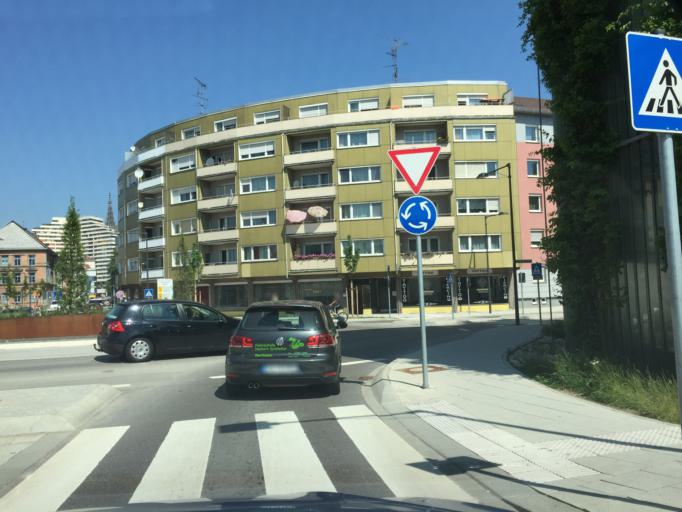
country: DE
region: Bavaria
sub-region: Swabia
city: Neu-Ulm
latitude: 48.3919
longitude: 10.0011
